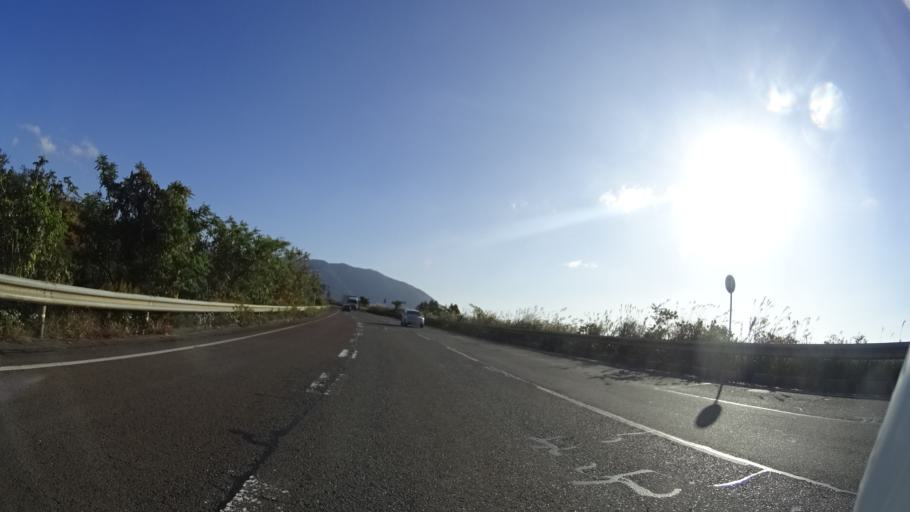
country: JP
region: Fukui
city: Tsuruga
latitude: 35.4551
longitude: 136.0406
